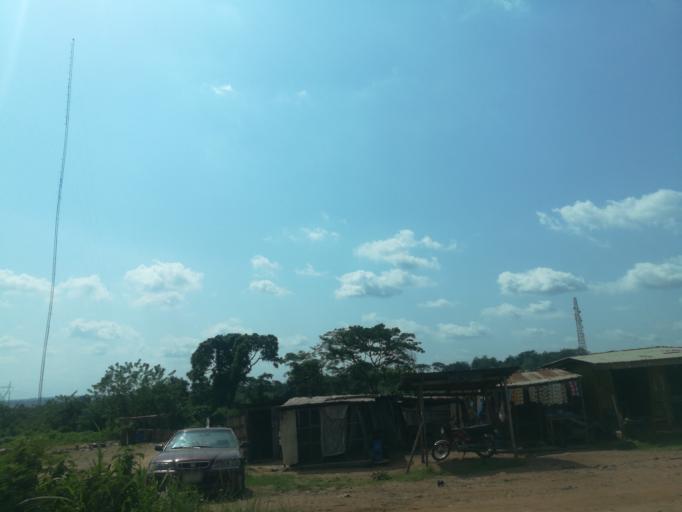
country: NG
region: Oyo
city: Moniya
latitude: 7.5240
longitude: 3.9119
